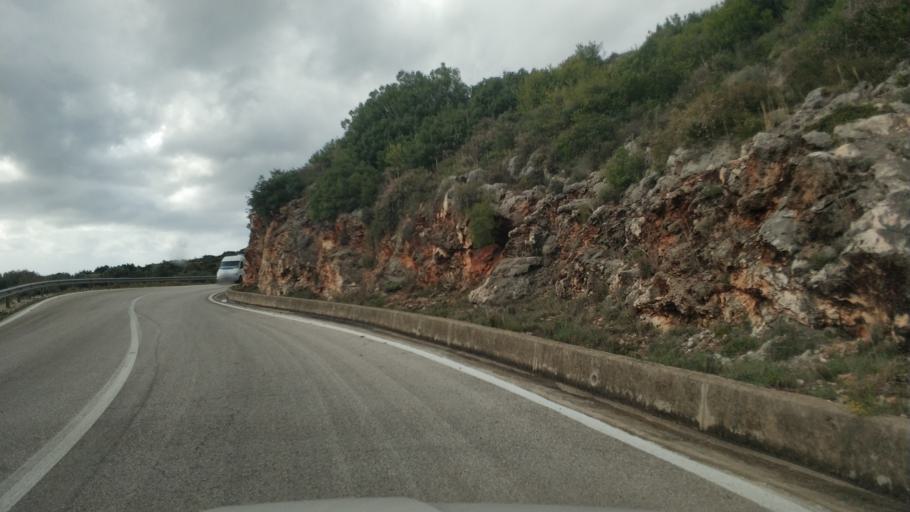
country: AL
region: Vlore
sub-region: Rrethi i Vlores
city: Vranisht
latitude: 40.1448
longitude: 19.6557
